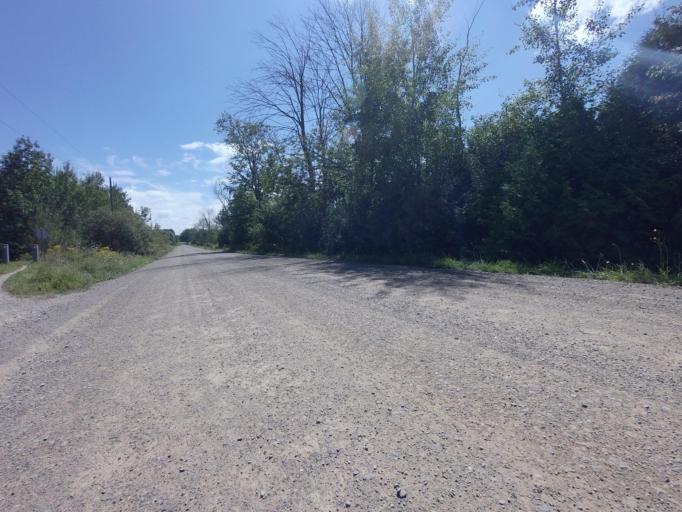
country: CA
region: Ontario
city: Orangeville
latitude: 43.7745
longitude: -80.1954
